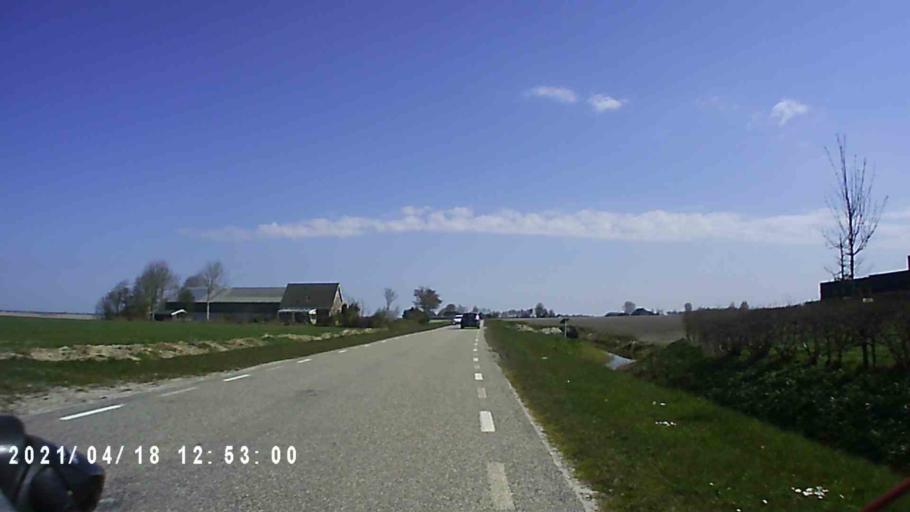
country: NL
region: Friesland
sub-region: Gemeente Dongeradeel
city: Anjum
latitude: 53.3826
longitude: 6.0642
